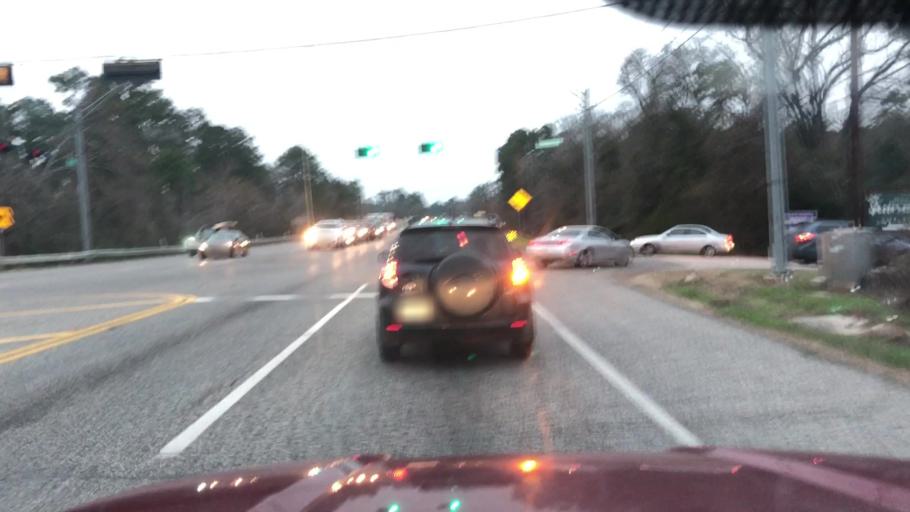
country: US
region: Texas
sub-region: Harris County
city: Tomball
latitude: 30.0815
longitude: -95.5640
